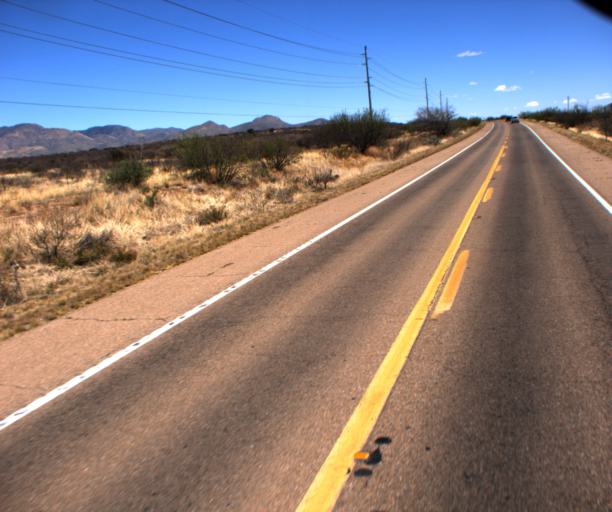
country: US
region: Arizona
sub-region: Cochise County
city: Naco
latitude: 31.3806
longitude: -110.0648
